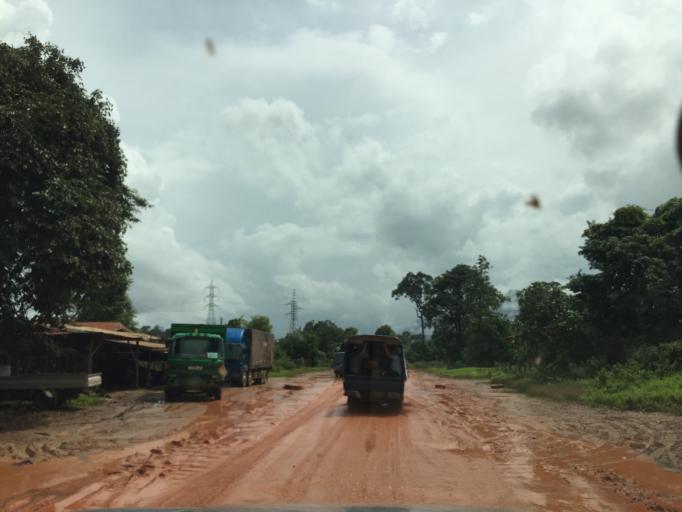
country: LA
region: Attapu
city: Attapu
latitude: 14.8121
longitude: 106.7820
